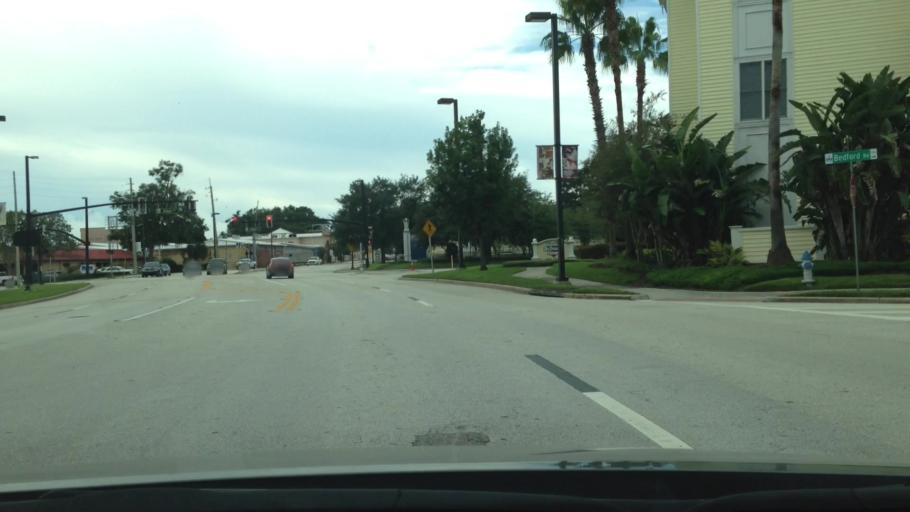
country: US
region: Florida
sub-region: Orange County
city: Fairview Shores
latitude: 28.5713
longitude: -81.3699
